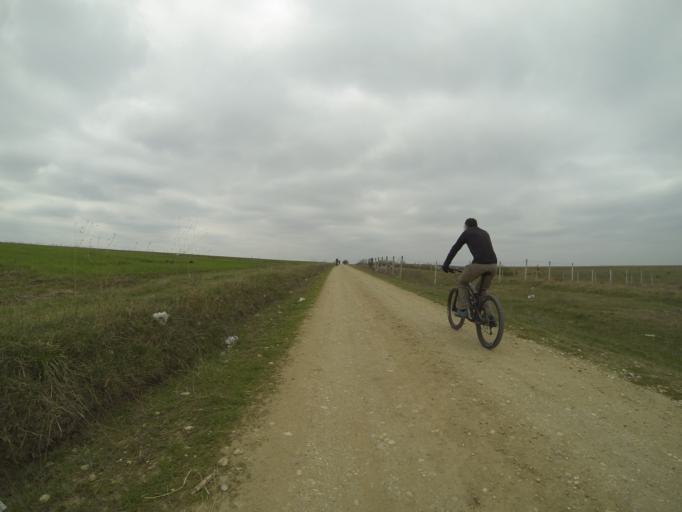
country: RO
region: Dolj
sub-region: Comuna Breasta
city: Breasta
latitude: 44.3406
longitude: 23.6650
